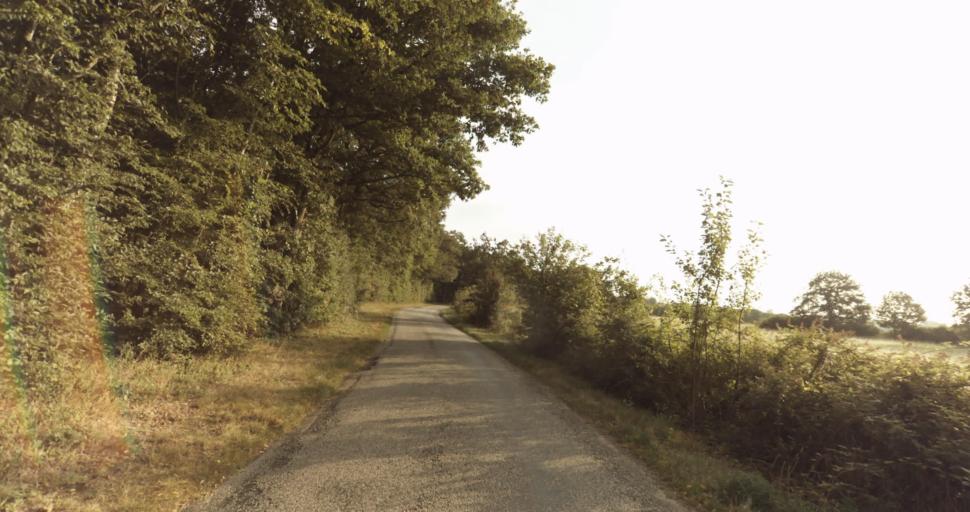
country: FR
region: Centre
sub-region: Departement d'Eure-et-Loir
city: Vert-en-Drouais
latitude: 48.7754
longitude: 1.3090
